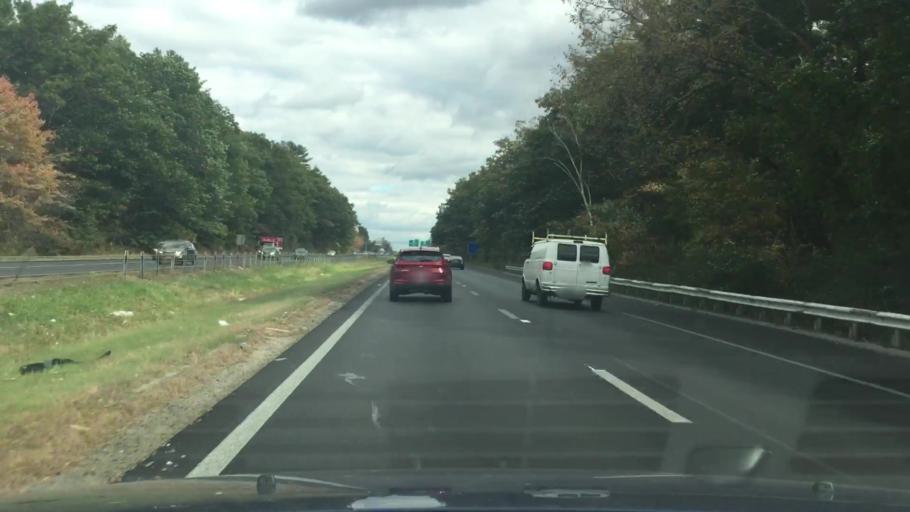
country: US
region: Massachusetts
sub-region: Essex County
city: Methuen
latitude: 42.7330
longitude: -71.1901
